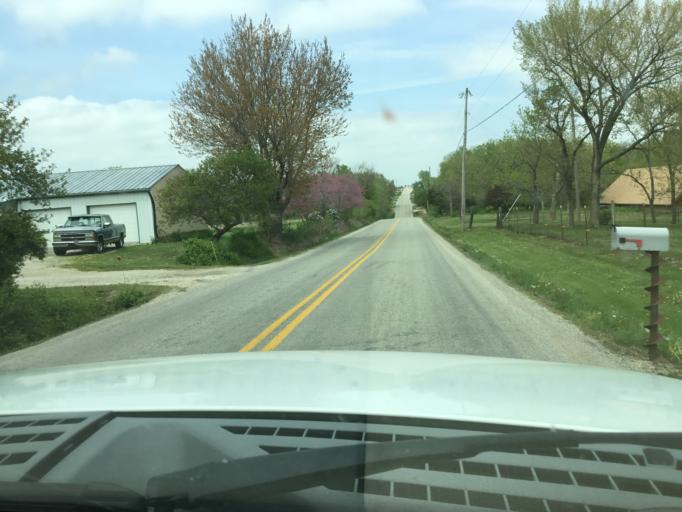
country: US
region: Kansas
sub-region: Shawnee County
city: Topeka
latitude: 38.9792
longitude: -95.6143
